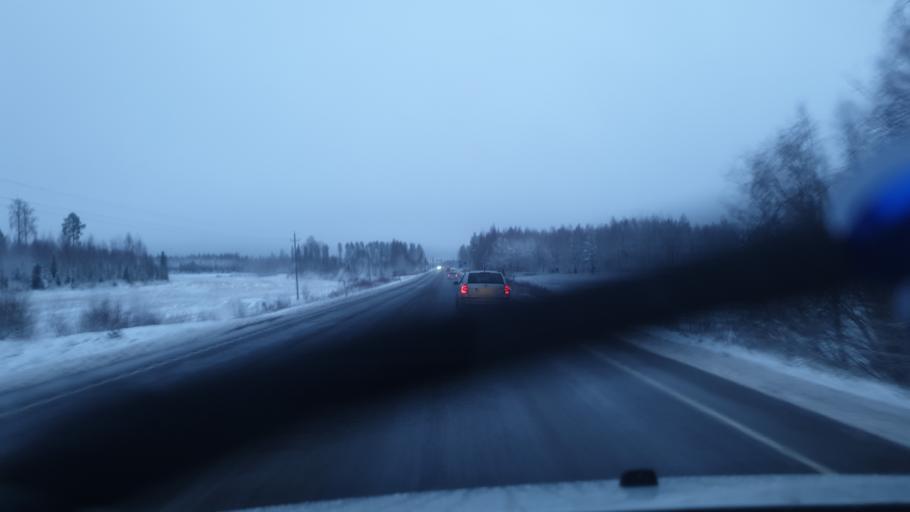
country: FI
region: Central Finland
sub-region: Saarijaervi-Viitasaari
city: Viitasaari
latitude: 63.1008
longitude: 25.8368
